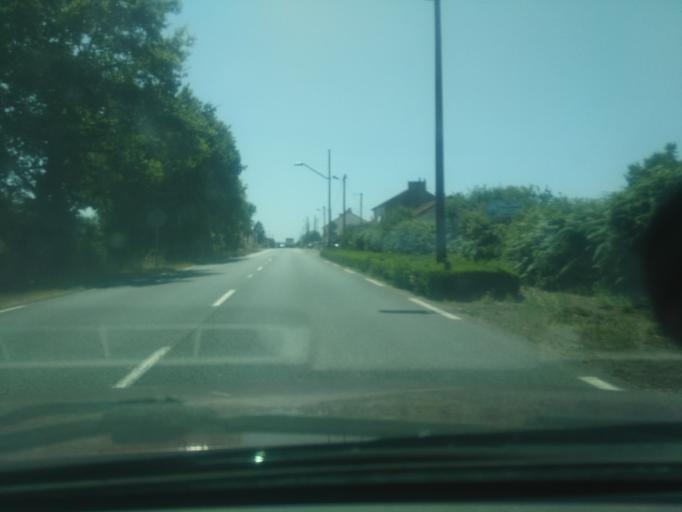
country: FR
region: Pays de la Loire
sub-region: Departement de la Vendee
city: La Ferriere
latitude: 46.7230
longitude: -1.2999
